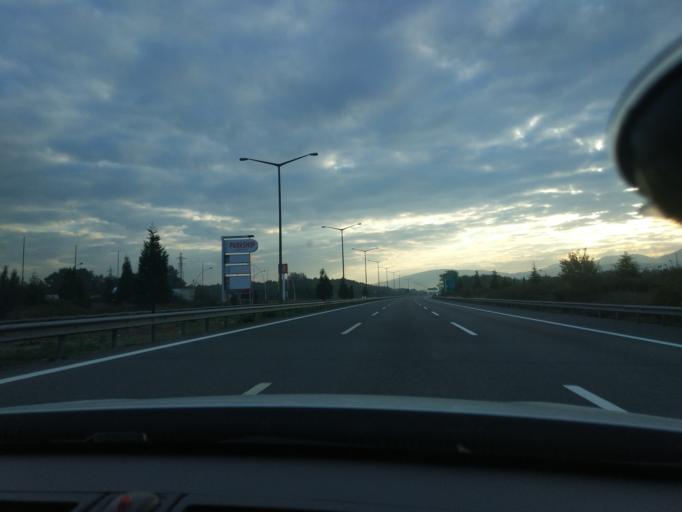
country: TR
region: Sakarya
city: Hendek
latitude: 40.7526
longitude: 30.6998
